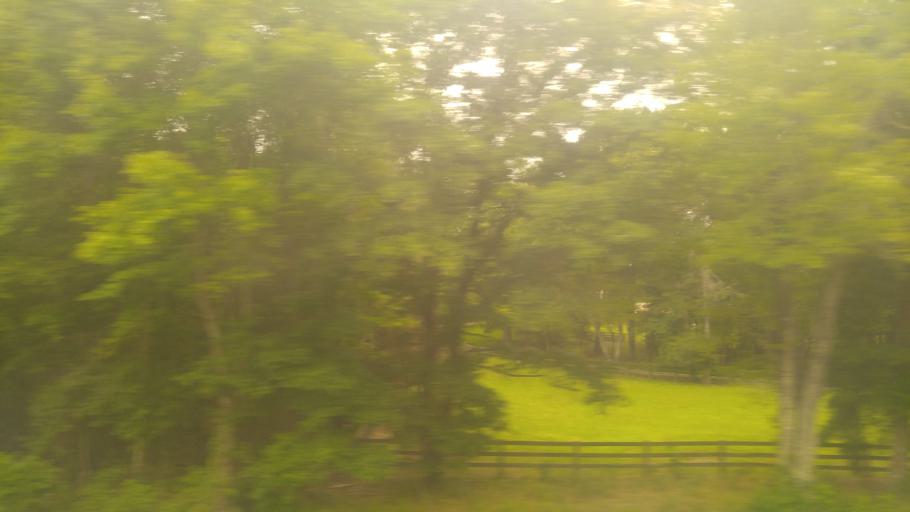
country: US
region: Virginia
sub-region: Hanover County
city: Ashland
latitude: 37.7364
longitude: -77.4883
